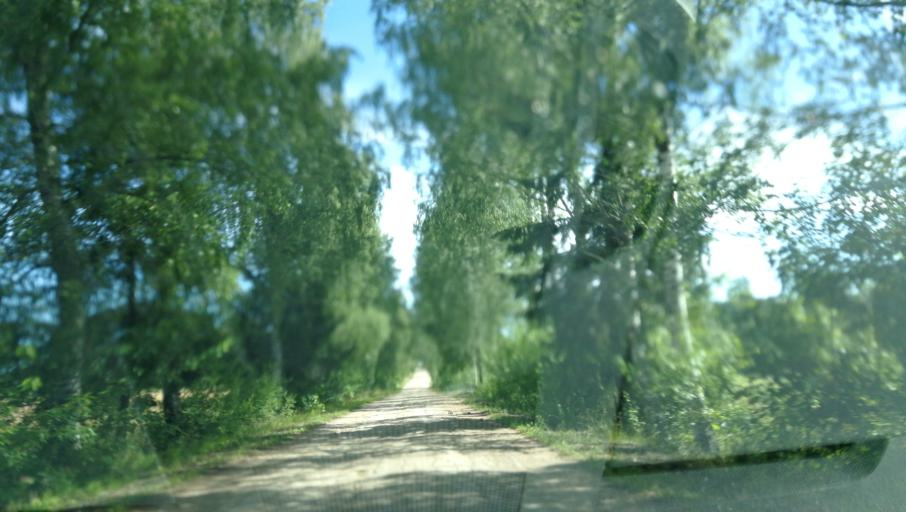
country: LV
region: Gulbenes Rajons
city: Gulbene
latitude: 57.1723
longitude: 26.8675
